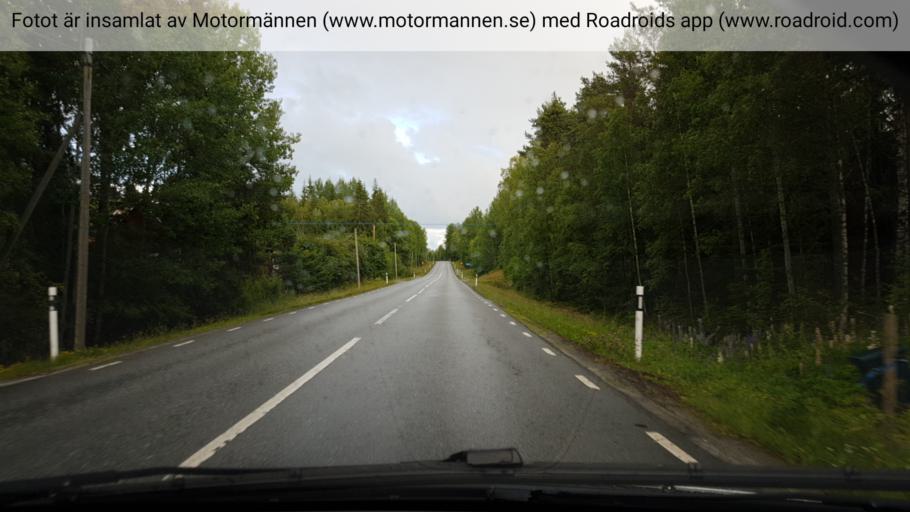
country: SE
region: OErebro
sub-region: Nora Kommun
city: As
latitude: 59.5210
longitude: 14.9014
